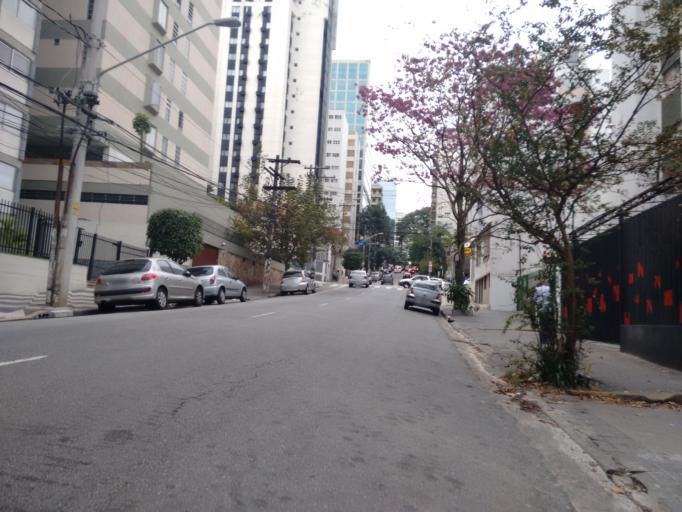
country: BR
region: Sao Paulo
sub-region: Sao Paulo
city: Sao Paulo
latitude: -23.5587
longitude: -46.6642
